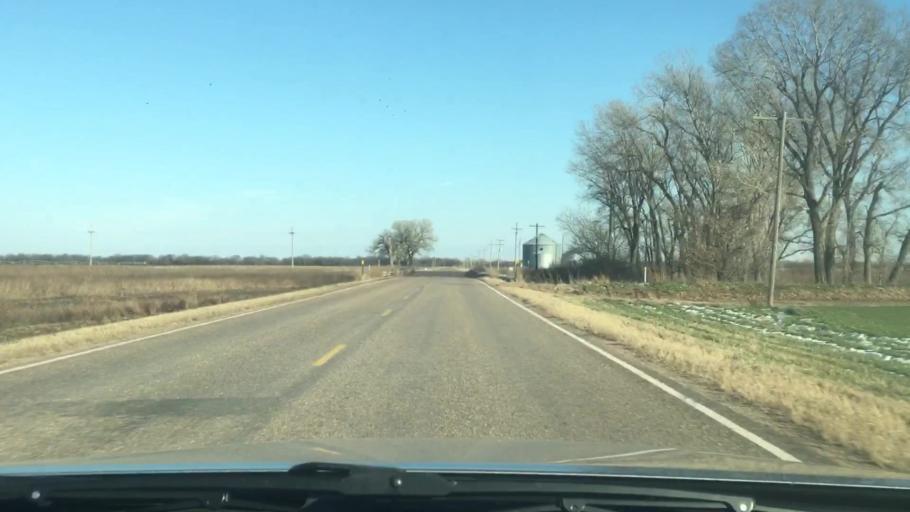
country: US
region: Kansas
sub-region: Rice County
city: Lyons
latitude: 38.2894
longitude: -98.1673
